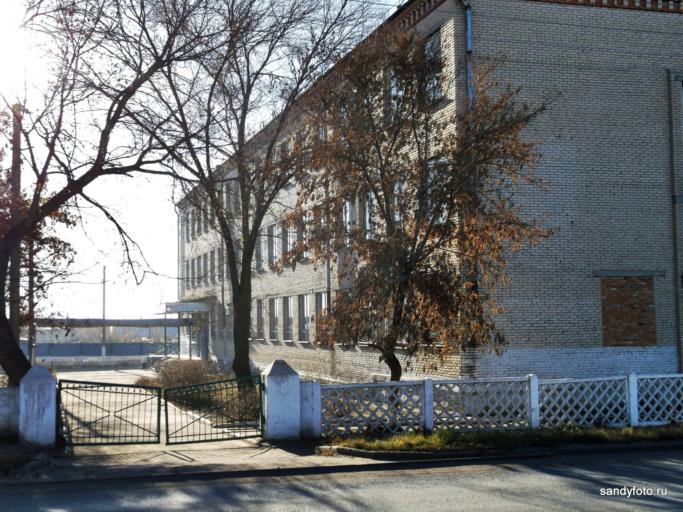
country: RU
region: Chelyabinsk
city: Troitsk
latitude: 54.0950
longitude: 61.5735
